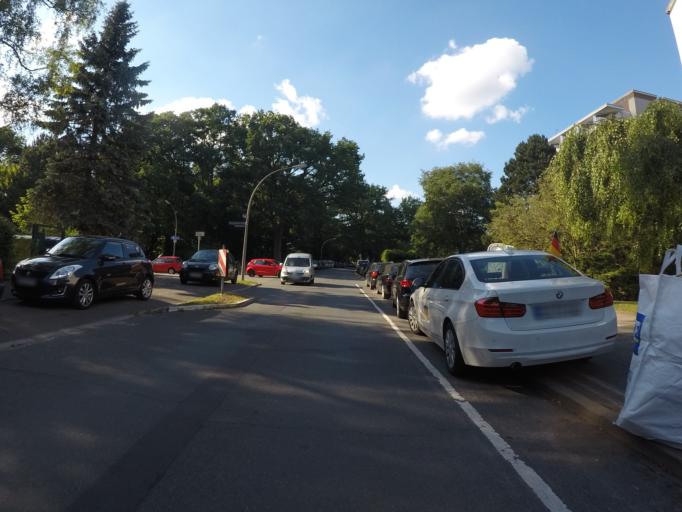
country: DE
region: Hamburg
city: Langenhorn
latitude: 53.6715
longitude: 10.0169
